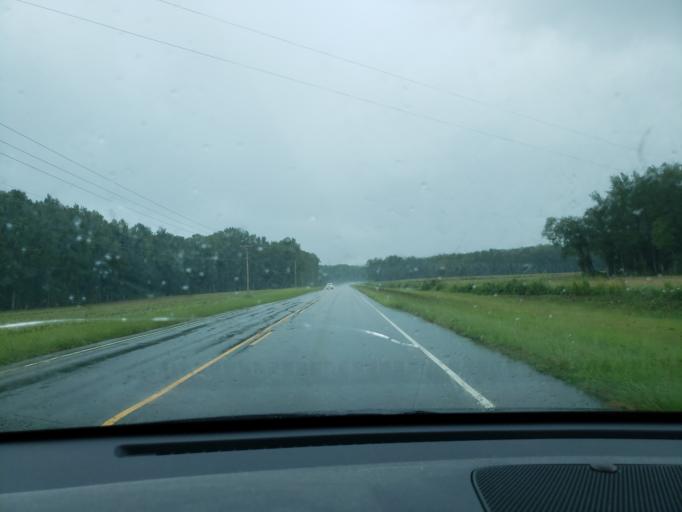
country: US
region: North Carolina
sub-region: Bladen County
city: Elizabethtown
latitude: 34.5192
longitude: -78.6524
